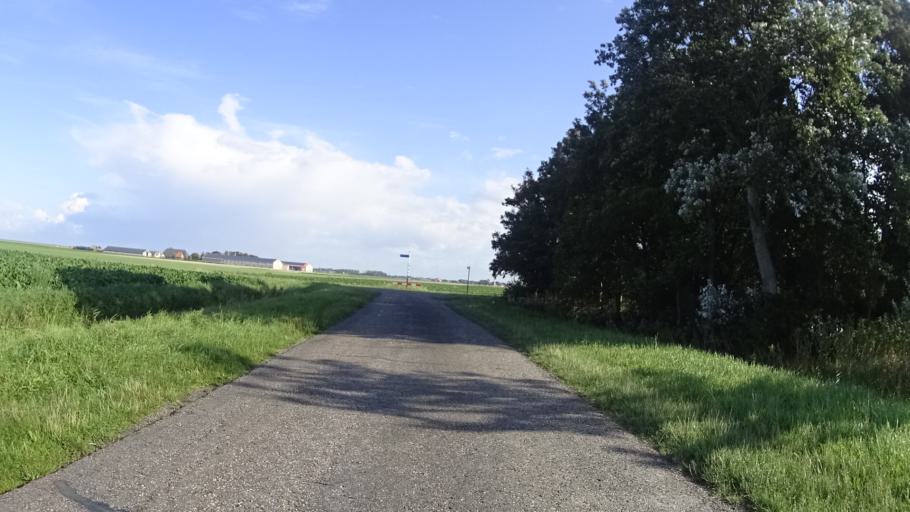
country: NL
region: Friesland
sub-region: Gemeente Harlingen
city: Harlingen
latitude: 53.1224
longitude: 5.4319
